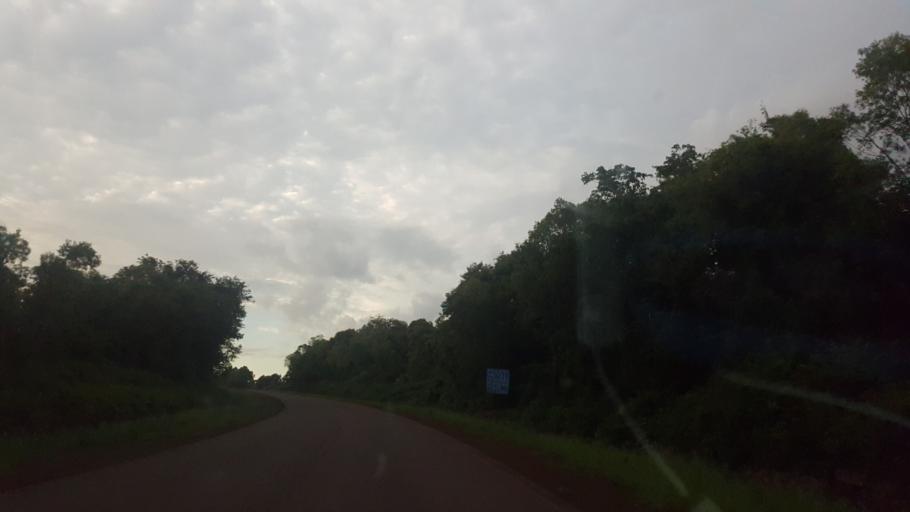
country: AR
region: Misiones
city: Dos de Mayo
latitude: -26.9353
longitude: -54.7195
